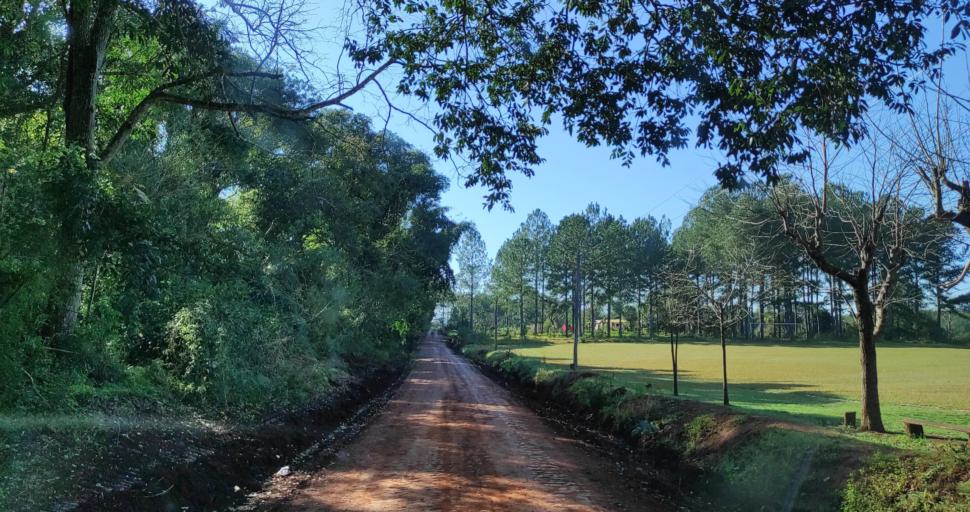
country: AR
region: Misiones
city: Capiovi
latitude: -26.8710
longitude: -55.0426
